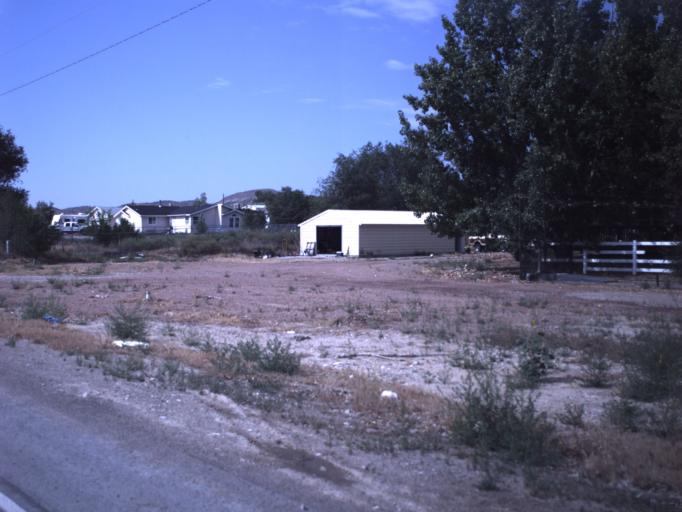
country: US
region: Utah
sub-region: Uintah County
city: Naples
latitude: 40.3708
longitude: -109.4984
